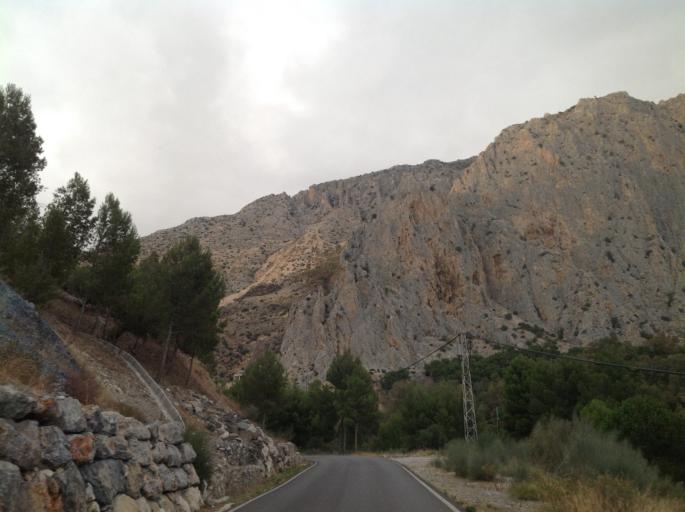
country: ES
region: Andalusia
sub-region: Provincia de Malaga
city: Carratraca
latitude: 36.9087
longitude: -4.7640
